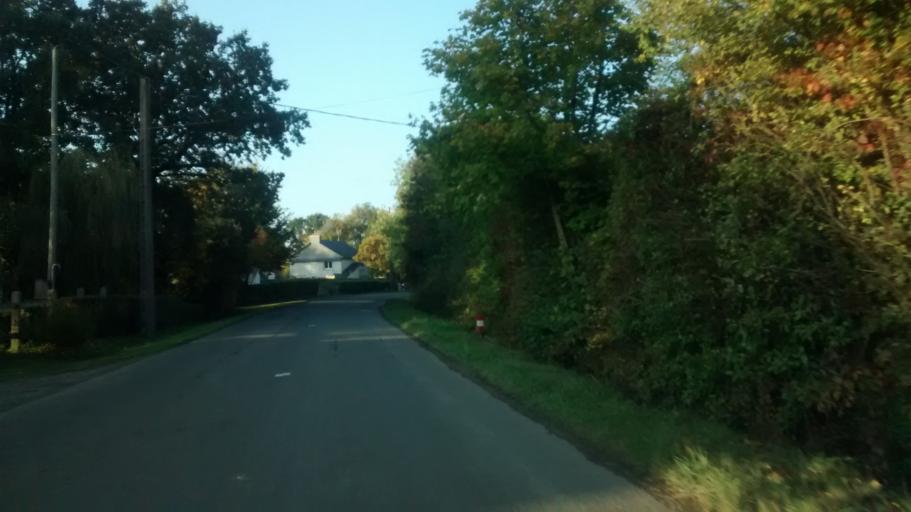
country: FR
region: Brittany
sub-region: Departement d'Ille-et-Vilaine
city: La Chapelle-Thouarault
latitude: 48.1100
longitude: -1.8494
